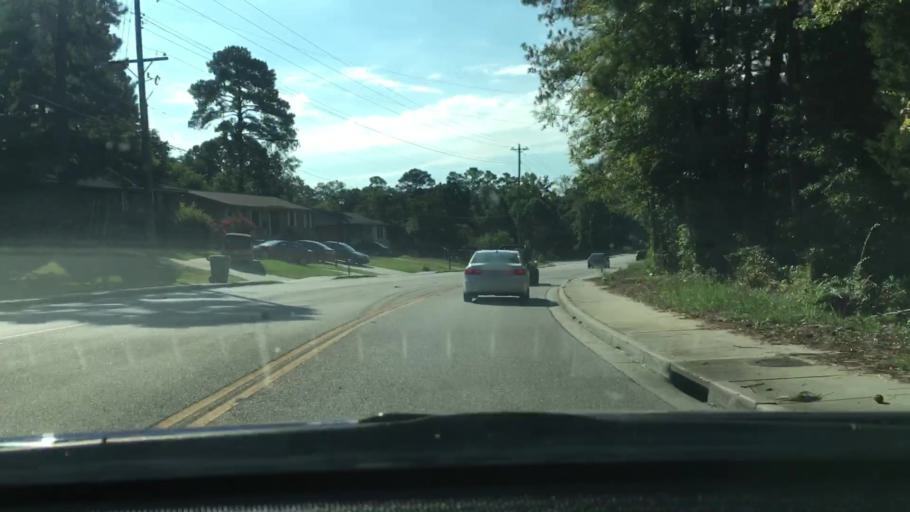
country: US
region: South Carolina
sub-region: Lexington County
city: Irmo
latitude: 34.1089
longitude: -81.1591
